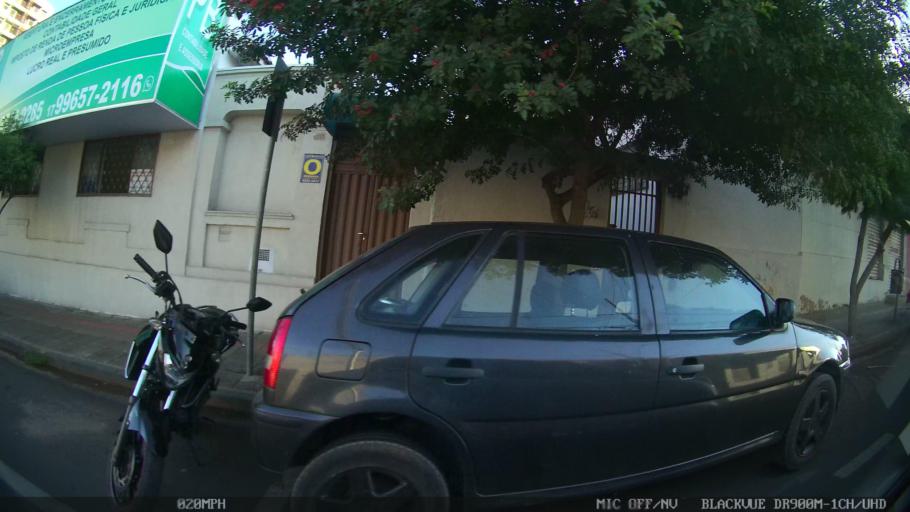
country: BR
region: Sao Paulo
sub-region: Sao Jose Do Rio Preto
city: Sao Jose do Rio Preto
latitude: -20.8037
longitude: -49.3834
